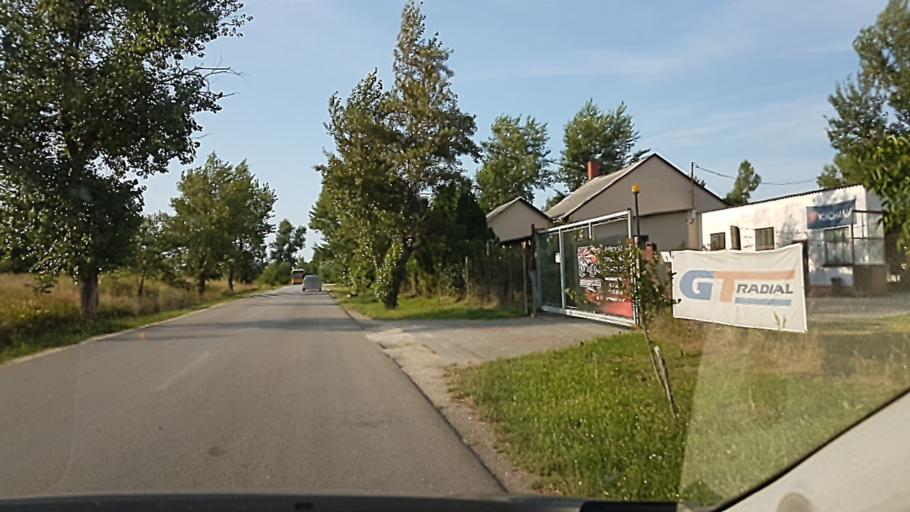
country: HU
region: Pest
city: Dunavarsany
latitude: 47.2594
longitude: 19.0625
